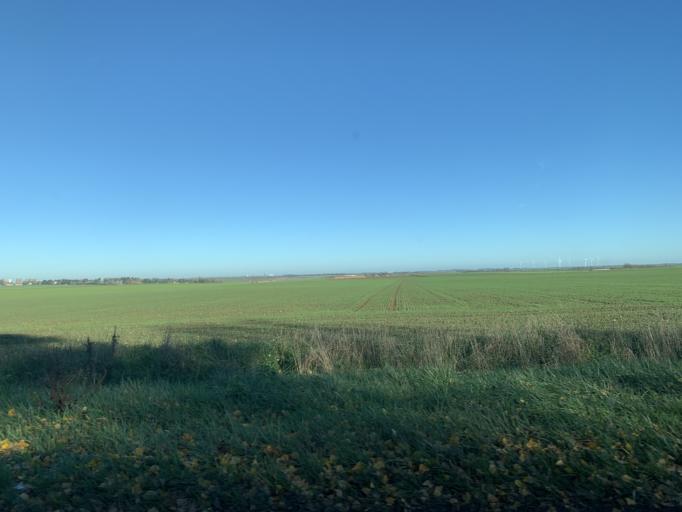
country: FR
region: Nord-Pas-de-Calais
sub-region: Departement du Nord
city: Escaudoeuvres
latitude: 50.1646
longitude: 3.2789
